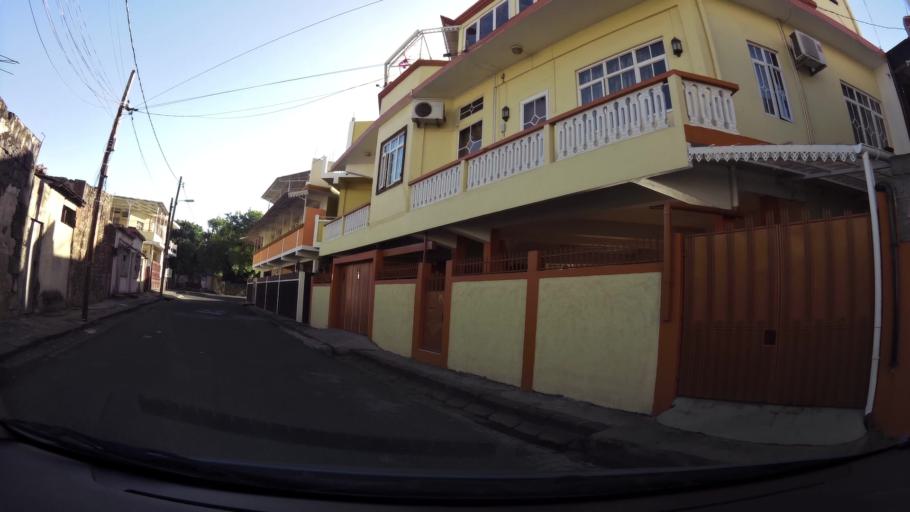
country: MU
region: Port Louis
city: Port Louis
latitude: -20.1644
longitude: 57.4915
